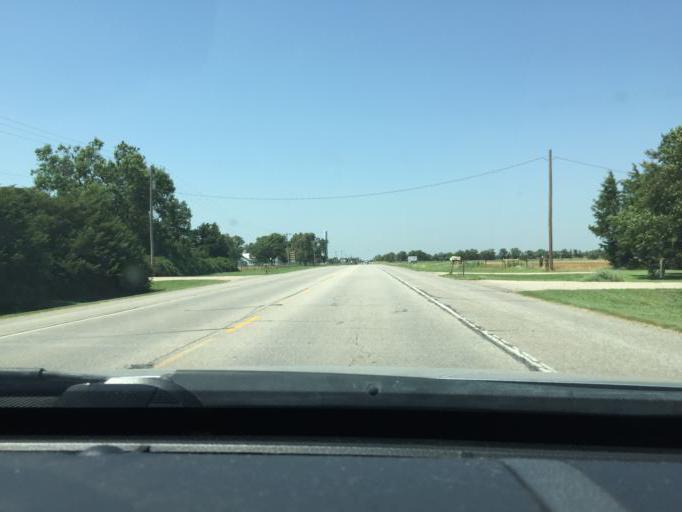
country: US
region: Kansas
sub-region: Reno County
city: Haven
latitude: 37.9480
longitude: -97.8668
